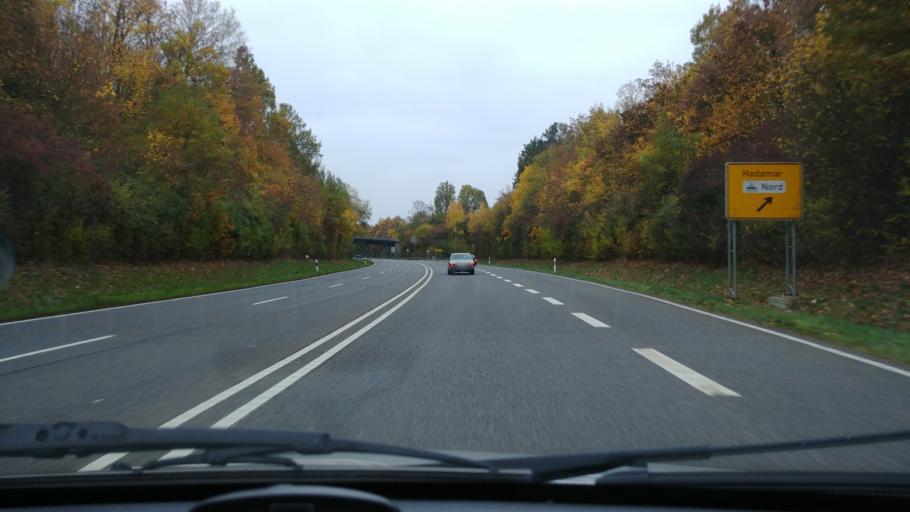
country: DE
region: Hesse
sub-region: Regierungsbezirk Giessen
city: Elz
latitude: 50.4658
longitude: 8.0570
